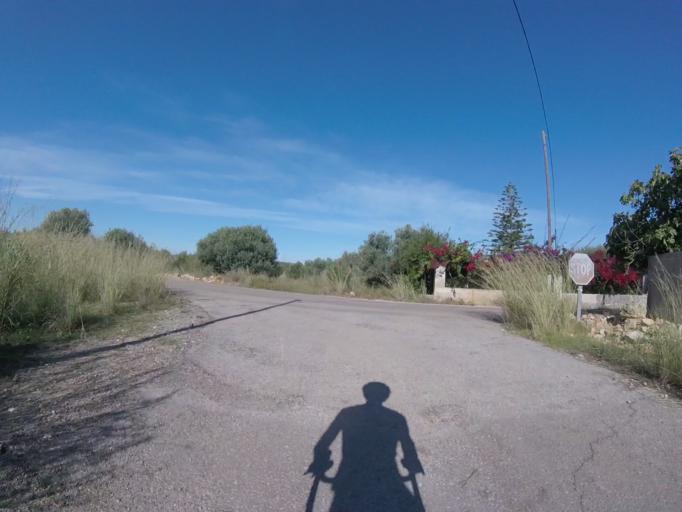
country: ES
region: Valencia
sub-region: Provincia de Castello
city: Torreblanca
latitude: 40.2088
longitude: 0.2382
